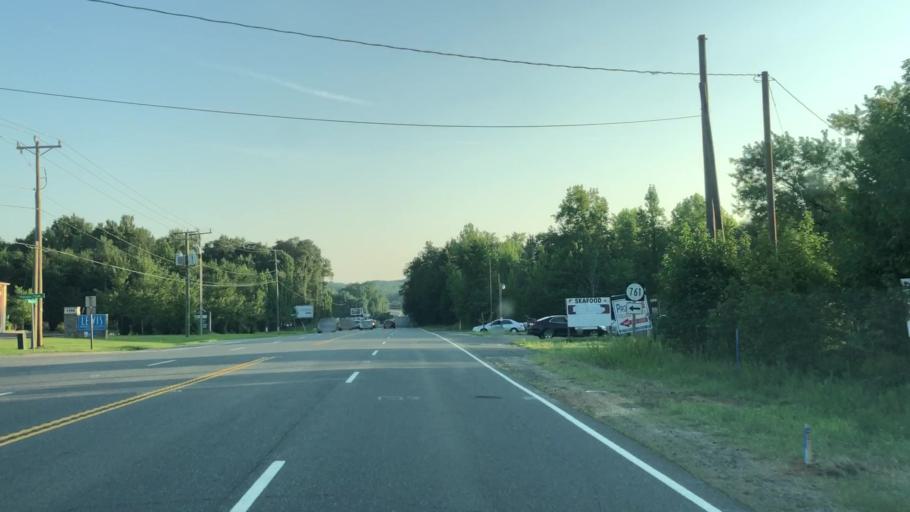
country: US
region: Virginia
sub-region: Stafford County
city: Stafford
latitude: 38.3824
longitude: -77.4457
